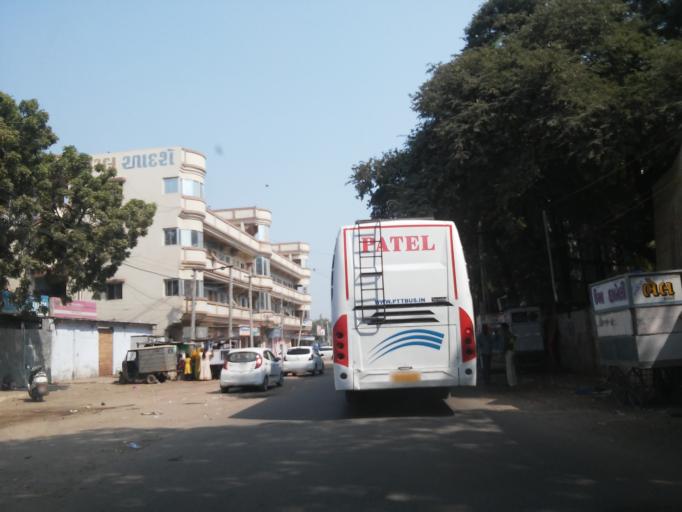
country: IN
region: Gujarat
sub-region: Kachchh
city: Mundra
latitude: 22.8430
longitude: 69.7243
